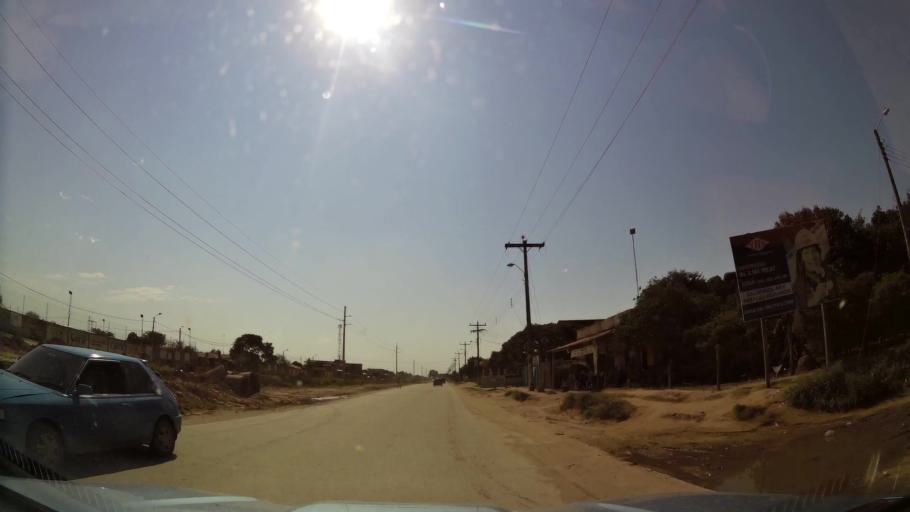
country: BO
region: Santa Cruz
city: Cotoca
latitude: -17.7431
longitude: -63.0976
